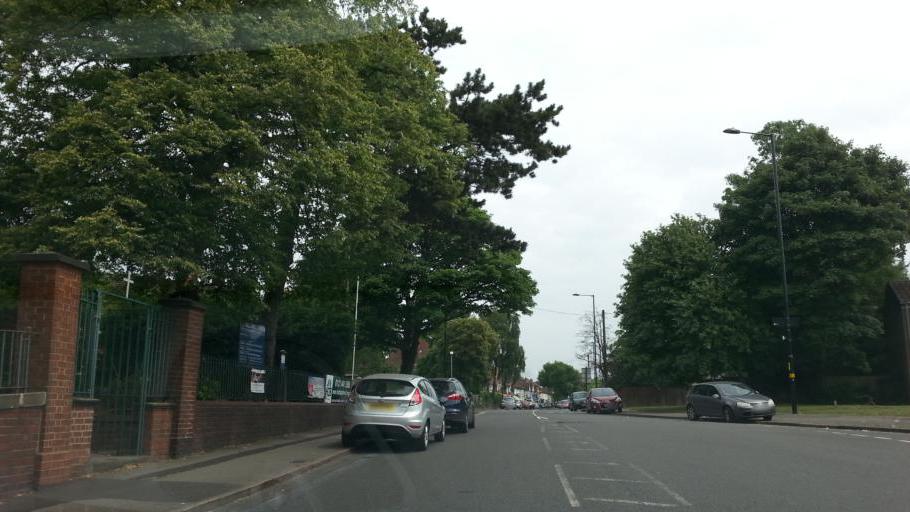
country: GB
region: England
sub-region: City and Borough of Birmingham
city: Birmingham
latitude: 52.4263
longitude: -1.9091
